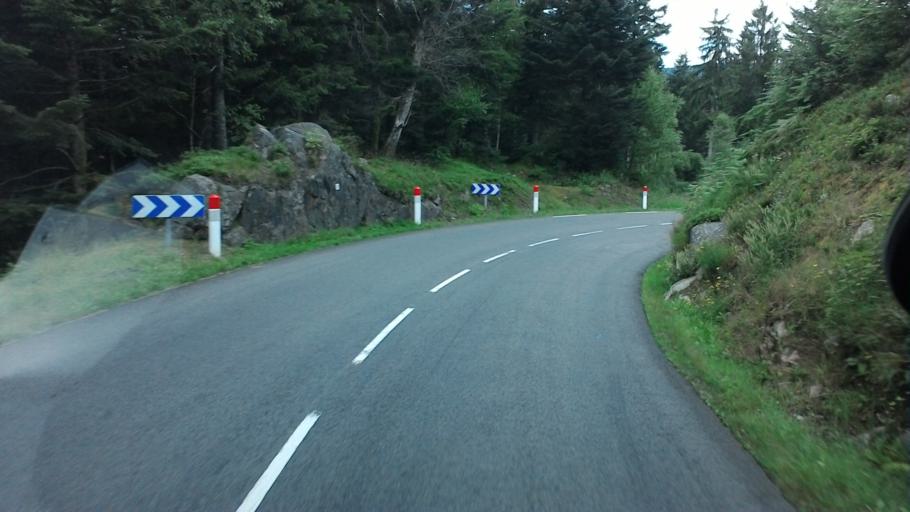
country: FR
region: Lorraine
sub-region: Departement des Vosges
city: Gerardmer
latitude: 48.0626
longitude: 6.8585
